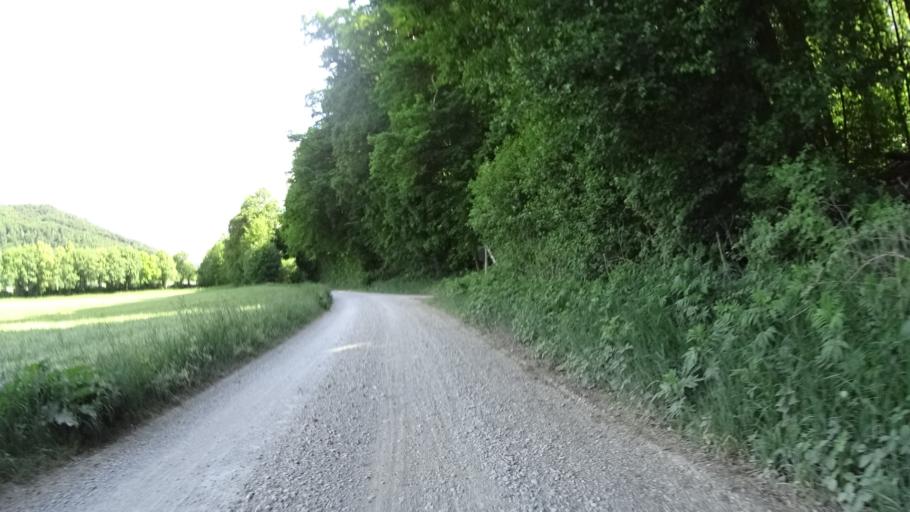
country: DE
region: Bavaria
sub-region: Regierungsbezirk Mittelfranken
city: Greding
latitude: 49.0159
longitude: 11.3558
